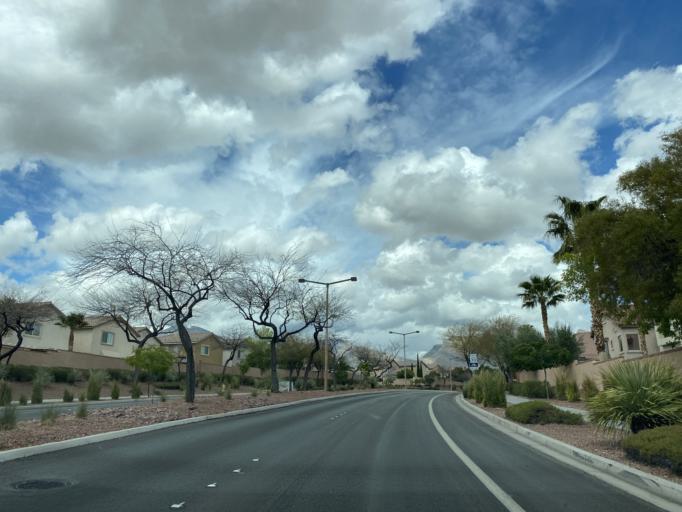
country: US
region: Nevada
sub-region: Clark County
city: Summerlin South
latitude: 36.1797
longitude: -115.3360
